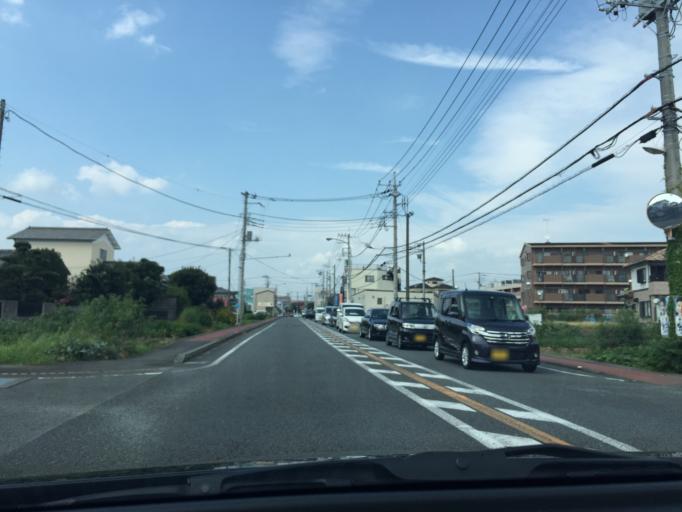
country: JP
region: Shizuoka
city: Mishima
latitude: 35.1262
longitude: 138.8984
